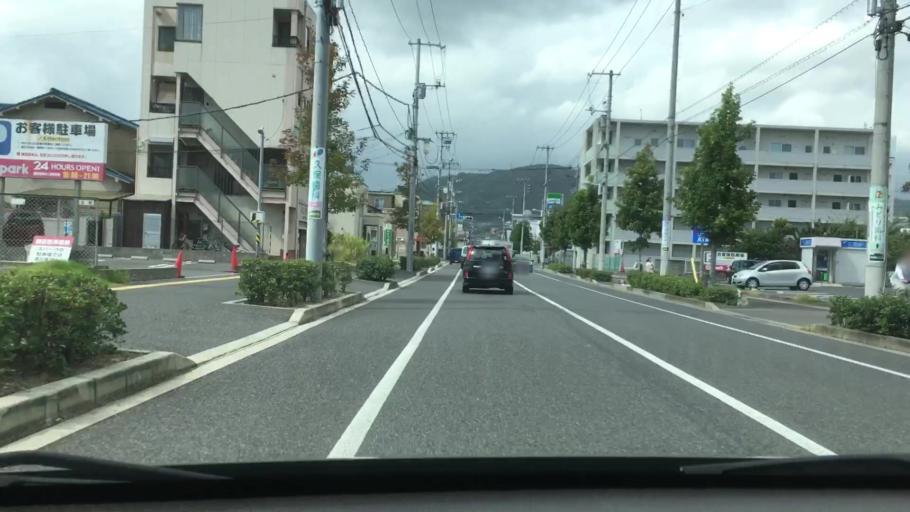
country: JP
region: Hiroshima
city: Hiroshima-shi
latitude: 34.3843
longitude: 132.4327
